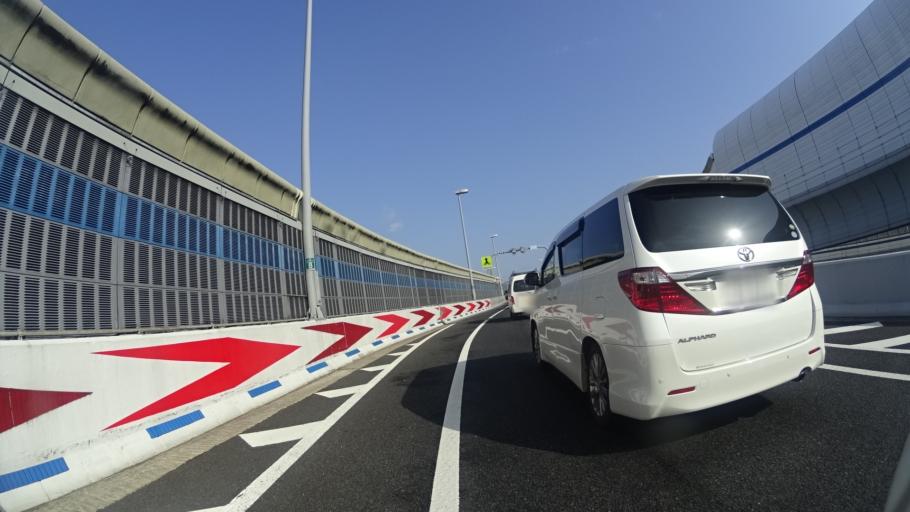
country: JP
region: Hyogo
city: Nishinomiya-hama
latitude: 34.7263
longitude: 135.3547
